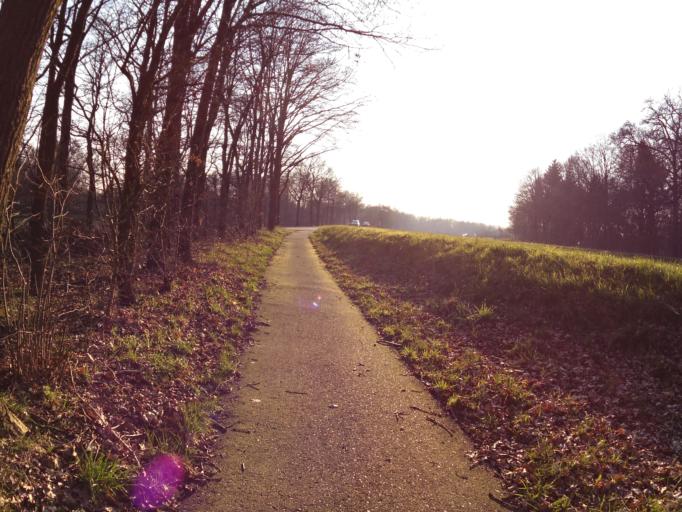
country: NL
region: North Brabant
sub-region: Gemeente Sint-Michielsgestel
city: Sint-Michielsgestel
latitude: 51.6979
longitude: 5.3720
